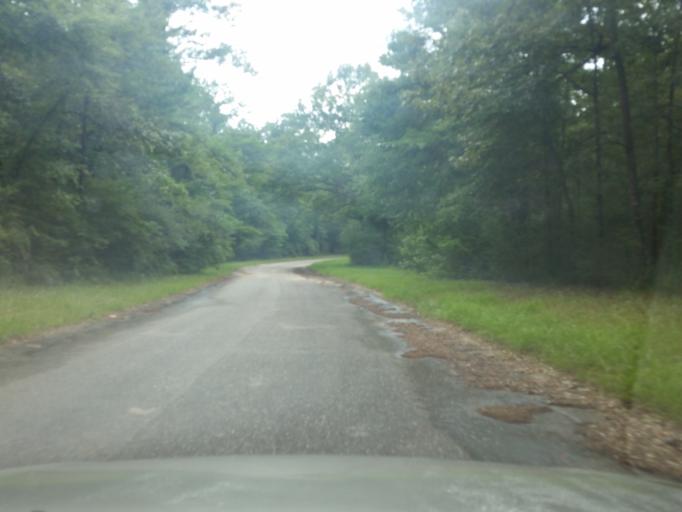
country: US
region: Alabama
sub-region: Baldwin County
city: Spanish Fort
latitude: 30.7319
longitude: -87.9100
